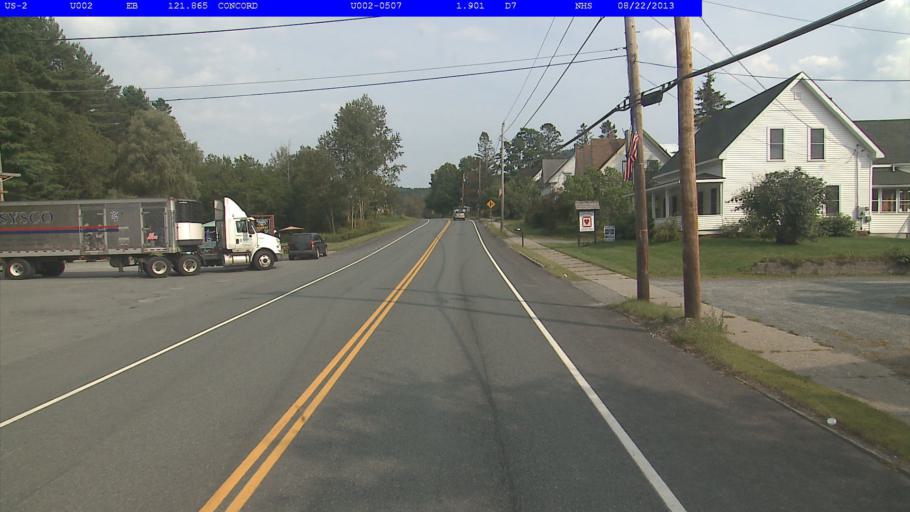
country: US
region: Vermont
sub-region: Caledonia County
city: St Johnsbury
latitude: 44.4295
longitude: -71.8920
